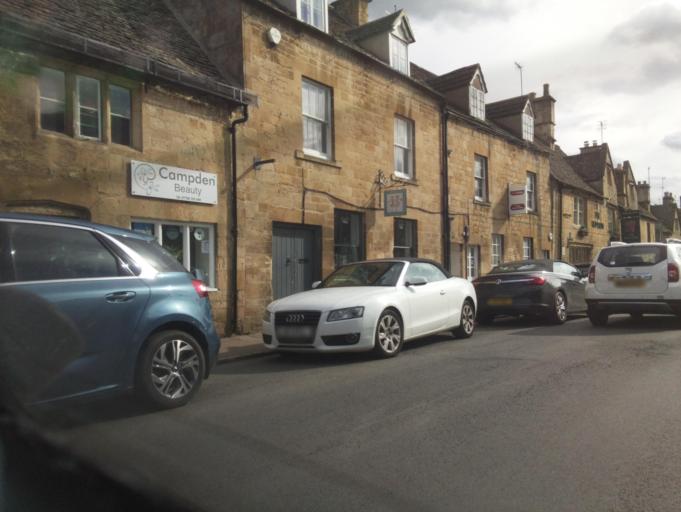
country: GB
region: England
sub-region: Gloucestershire
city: Chipping Campden
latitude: 52.0499
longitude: -1.7827
